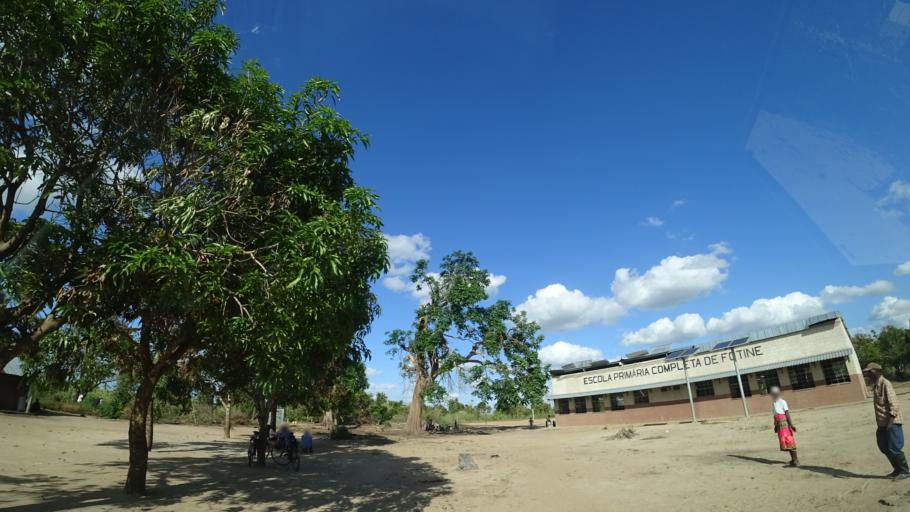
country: MZ
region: Sofala
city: Dondo
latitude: -19.4334
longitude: 34.7320
